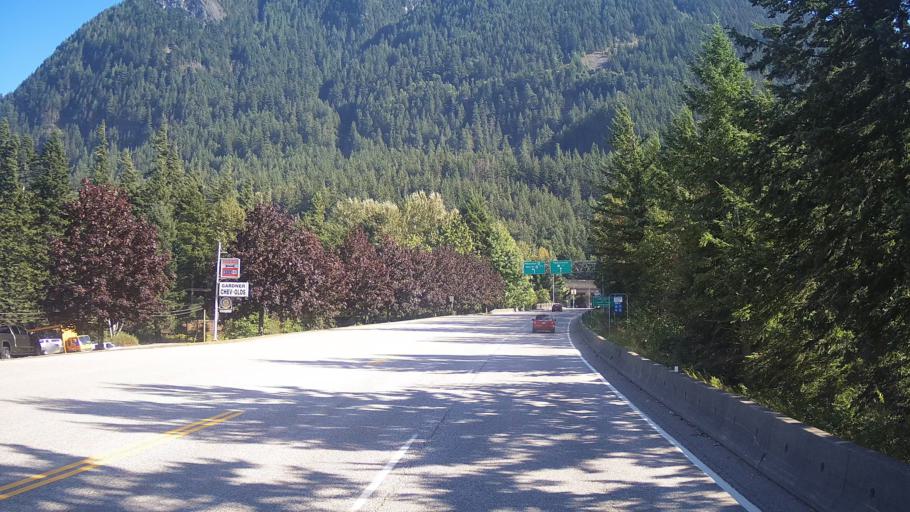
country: CA
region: British Columbia
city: Hope
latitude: 49.3761
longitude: -121.4427
